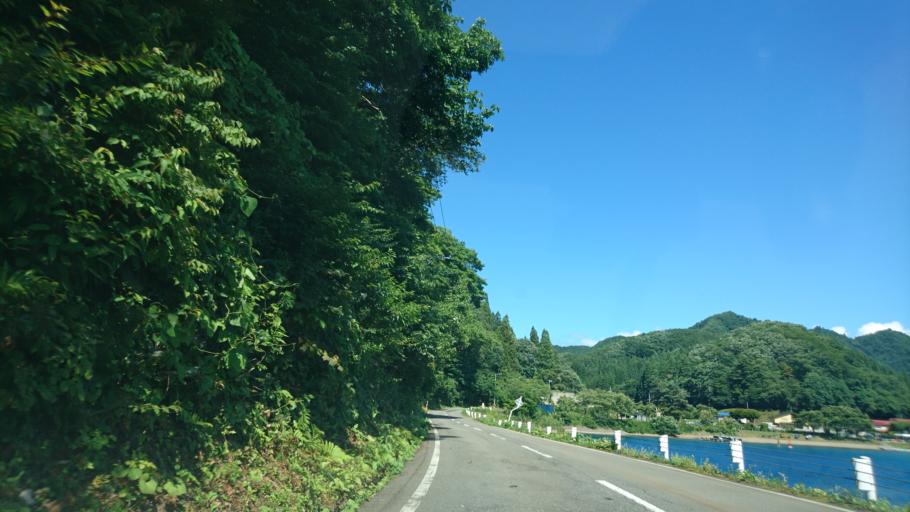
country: JP
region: Akita
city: Kakunodatemachi
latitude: 39.7106
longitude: 140.6361
